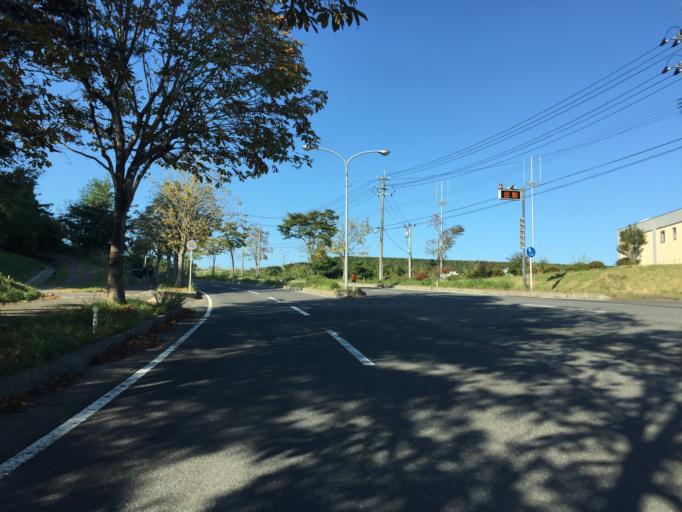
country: JP
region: Fukushima
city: Fukushima-shi
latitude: 37.6869
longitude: 140.4760
